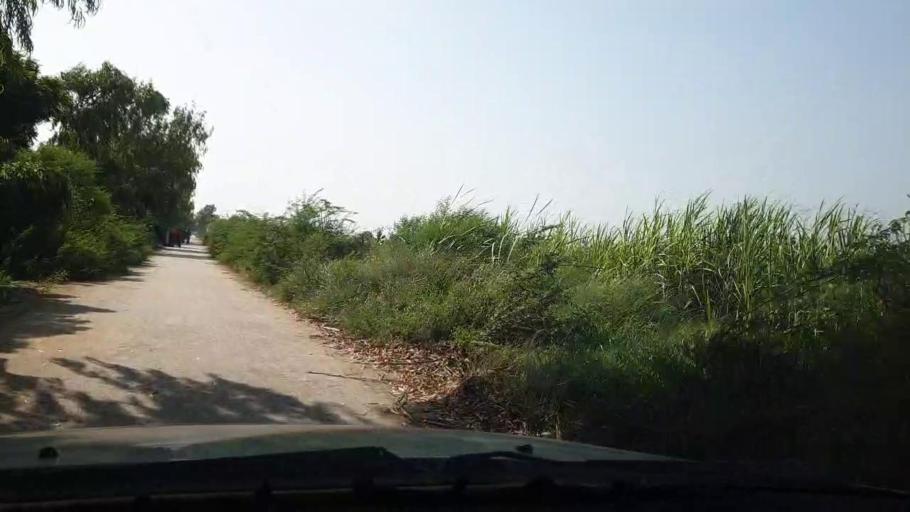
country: PK
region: Sindh
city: Chambar
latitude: 25.2447
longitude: 68.9190
